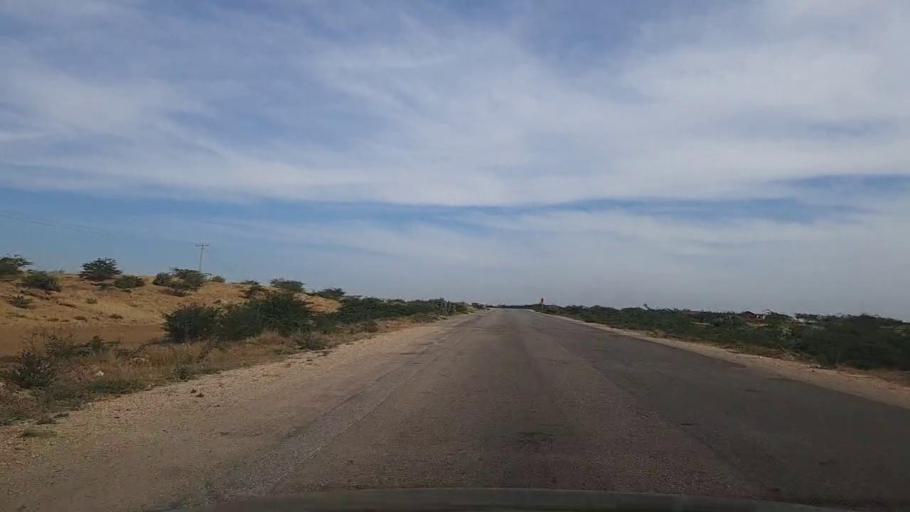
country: PK
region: Sindh
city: Thatta
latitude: 24.8663
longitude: 68.0303
